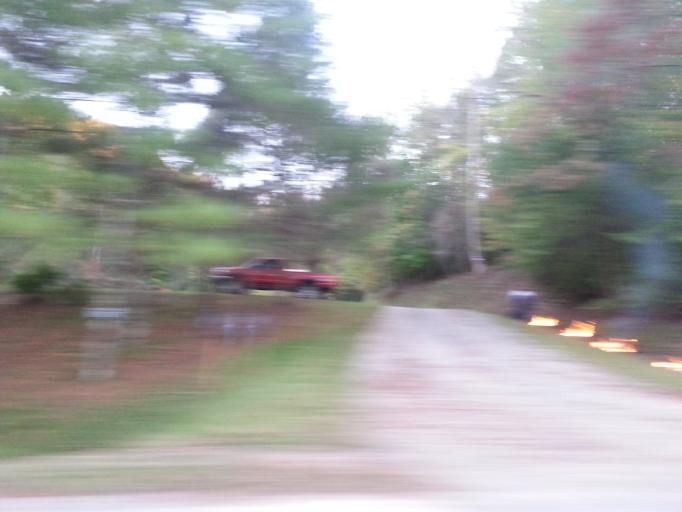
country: US
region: Tennessee
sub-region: Blount County
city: Wildwood
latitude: 35.7769
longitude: -83.7866
